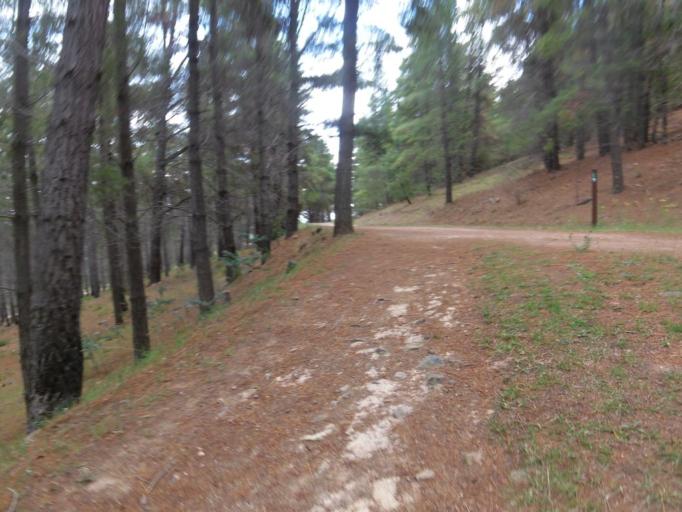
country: AU
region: Australian Capital Territory
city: Macarthur
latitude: -35.3647
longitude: 149.1139
